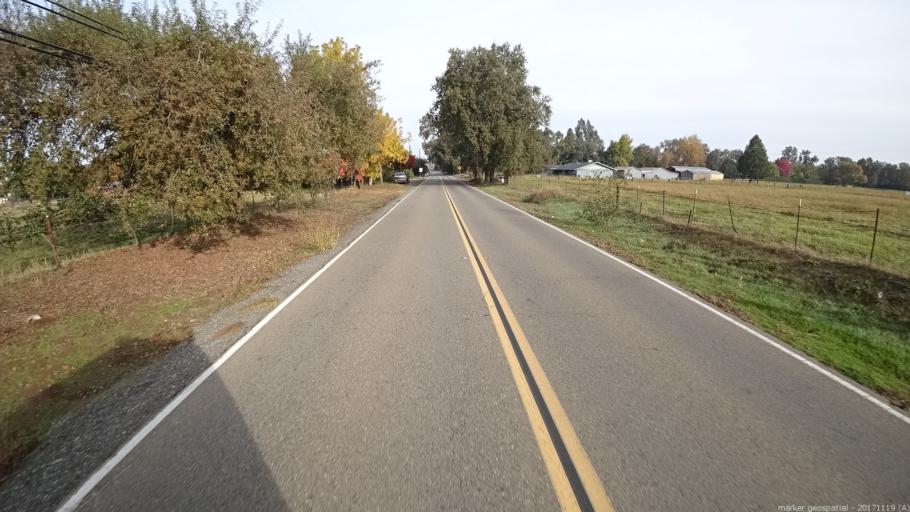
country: US
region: California
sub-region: Shasta County
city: Anderson
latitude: 40.5033
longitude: -122.3241
